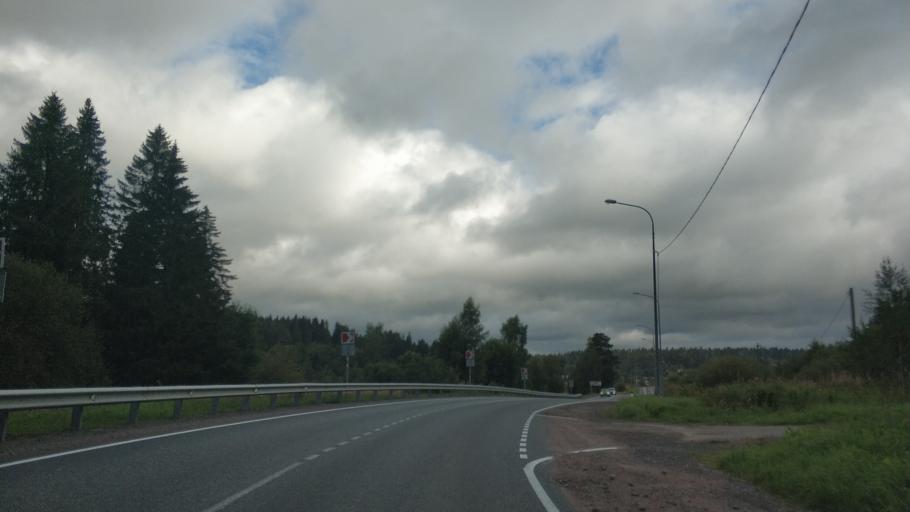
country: RU
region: Republic of Karelia
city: Khelyulya
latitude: 61.7553
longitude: 30.6566
